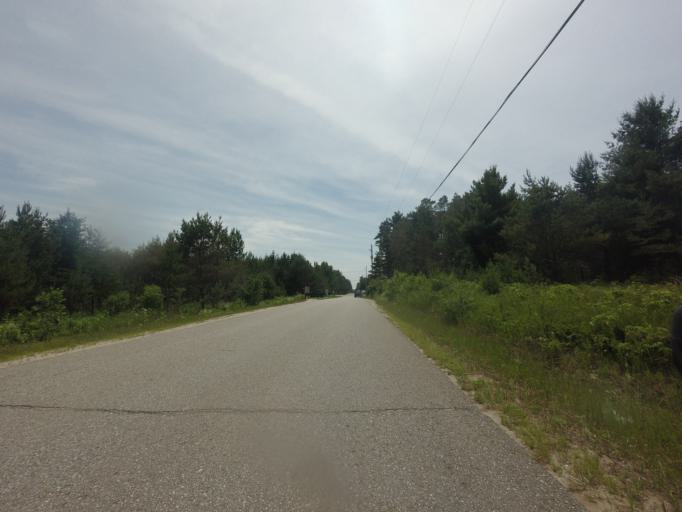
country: CA
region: Quebec
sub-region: Outaouais
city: Wakefield
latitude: 45.9524
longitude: -76.0603
